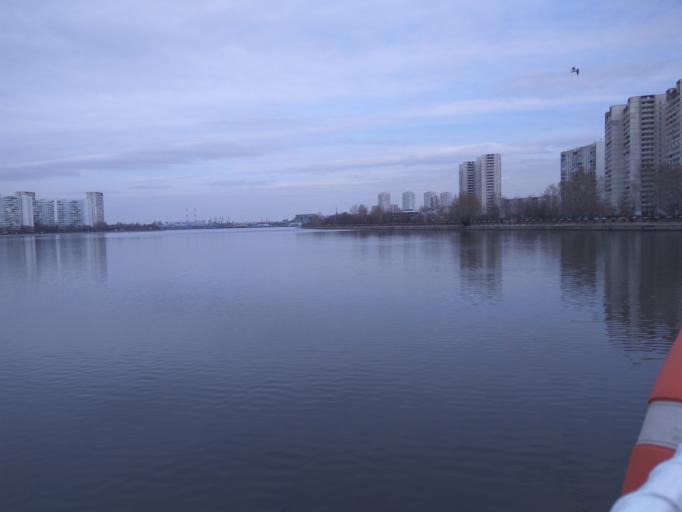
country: RU
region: Moscow
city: Mar'ino
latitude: 55.6756
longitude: 37.7139
